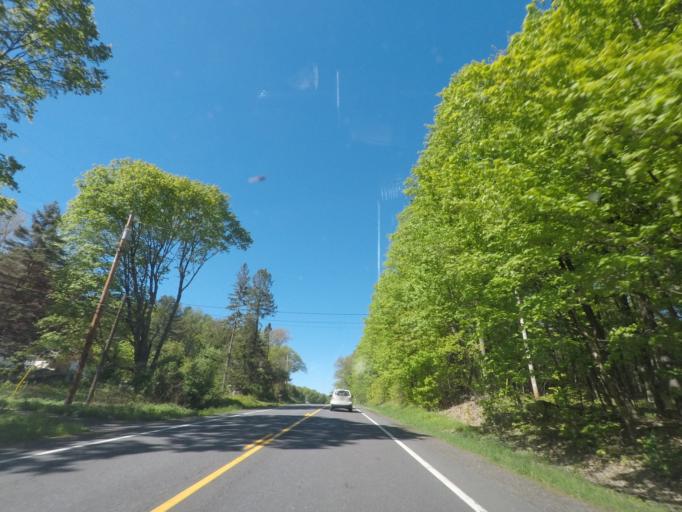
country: US
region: New York
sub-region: Greene County
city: Jefferson Heights
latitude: 42.2464
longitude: -73.8633
